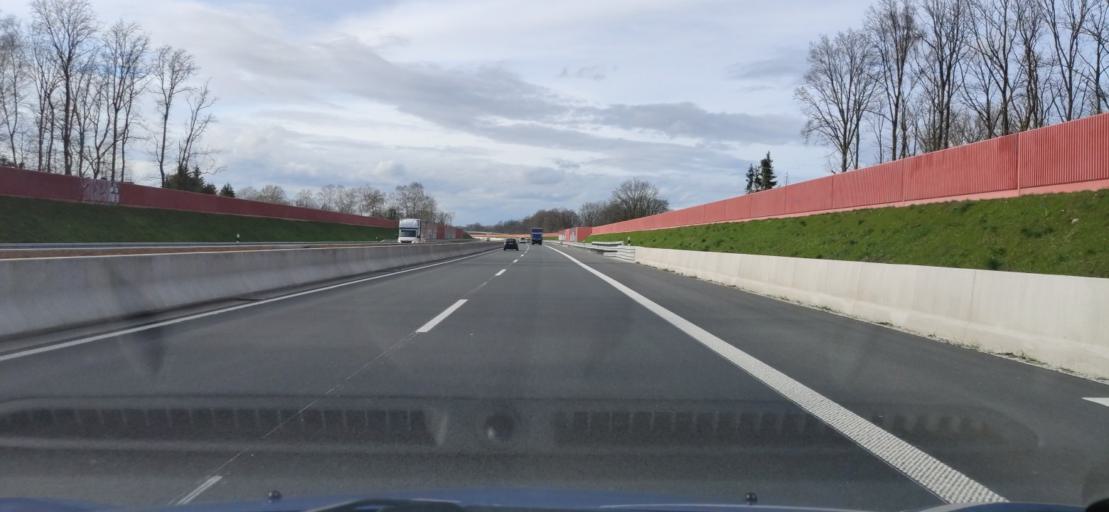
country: DE
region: North Rhine-Westphalia
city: Halle
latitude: 52.0610
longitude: 8.3274
